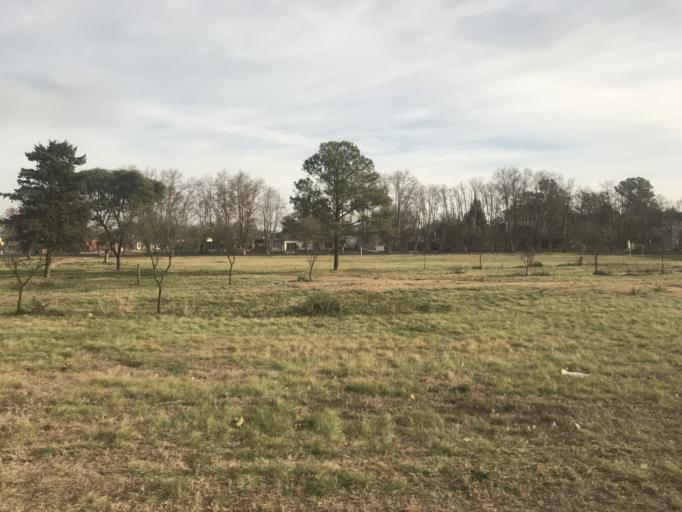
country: AR
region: Cordoba
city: Pilar
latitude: -31.6831
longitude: -63.8849
